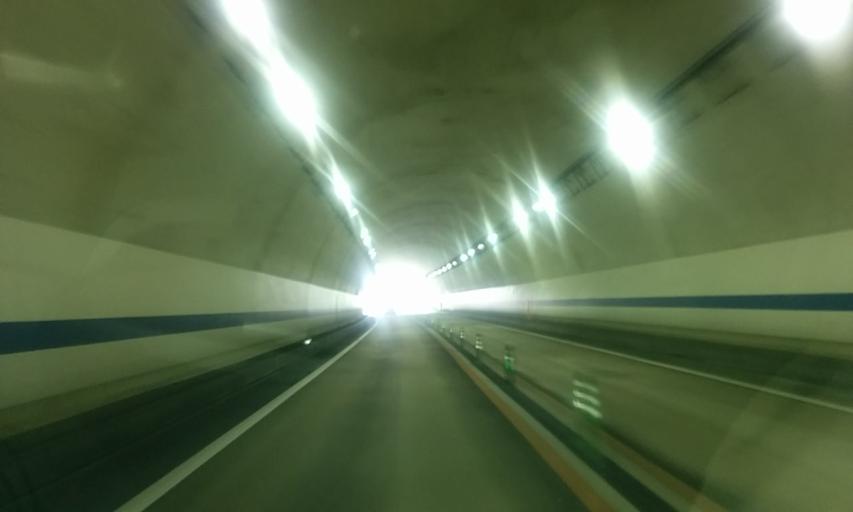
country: JP
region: Kyoto
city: Ayabe
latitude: 35.4096
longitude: 135.2262
